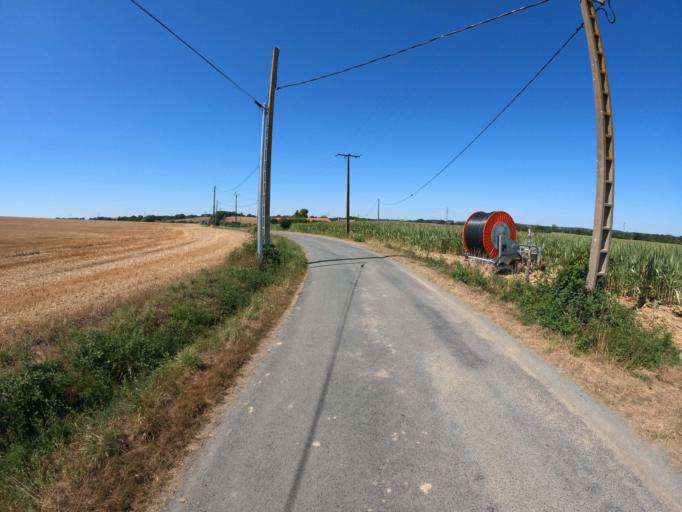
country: FR
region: Pays de la Loire
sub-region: Departement de Maine-et-Loire
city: Saint-Christophe-du-Bois
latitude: 47.0349
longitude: -0.9482
